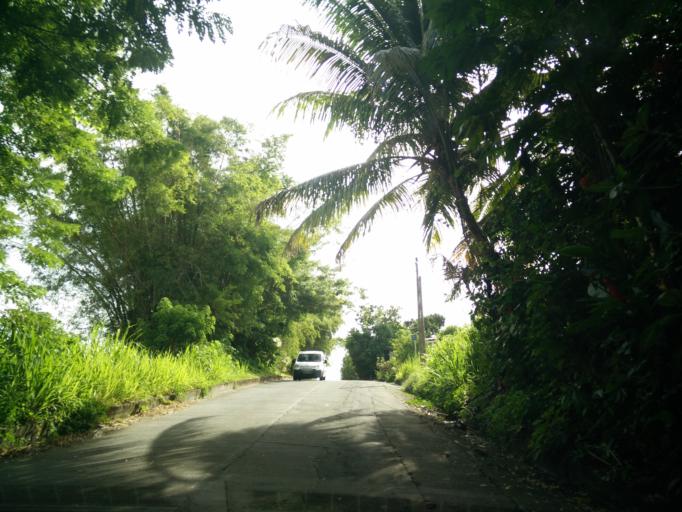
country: MQ
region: Martinique
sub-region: Martinique
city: Saint-Pierre
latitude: 14.7560
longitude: -61.1645
